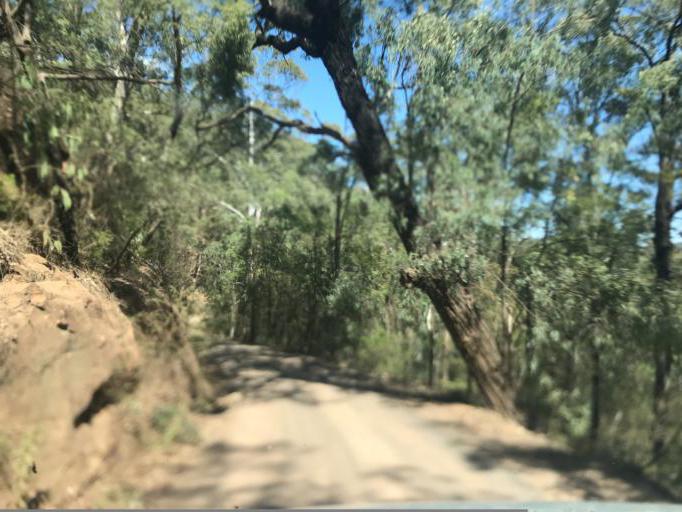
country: AU
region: New South Wales
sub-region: Wyong Shire
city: Little Jilliby
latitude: -33.1561
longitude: 151.0779
